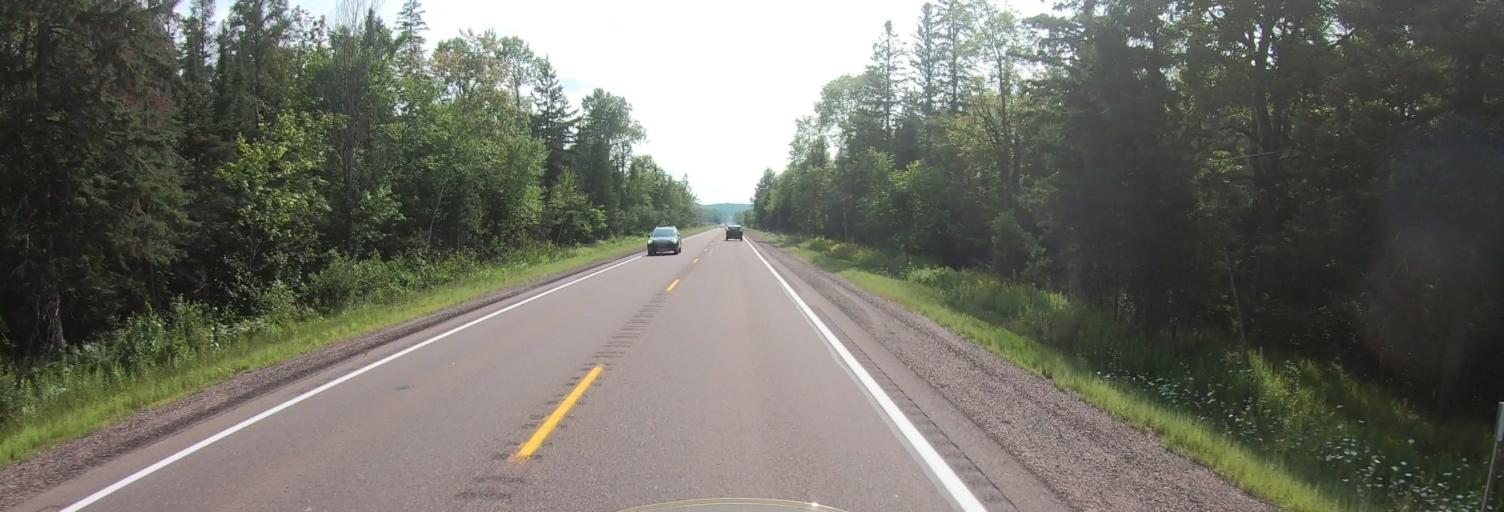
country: US
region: Michigan
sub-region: Gogebic County
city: Wakefield
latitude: 46.5066
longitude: -89.8955
